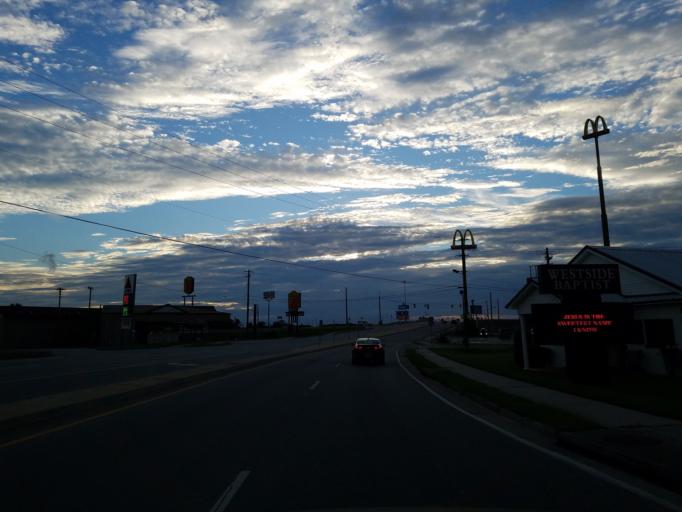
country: US
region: Georgia
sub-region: Cook County
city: Adel
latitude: 31.1439
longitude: -83.4339
